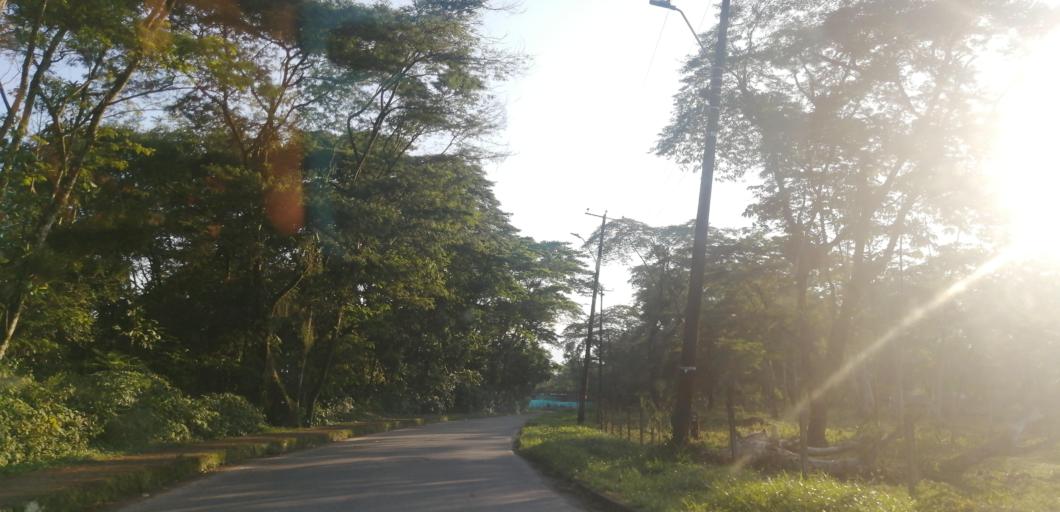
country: CO
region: Meta
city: Acacias
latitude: 3.9780
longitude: -73.7589
